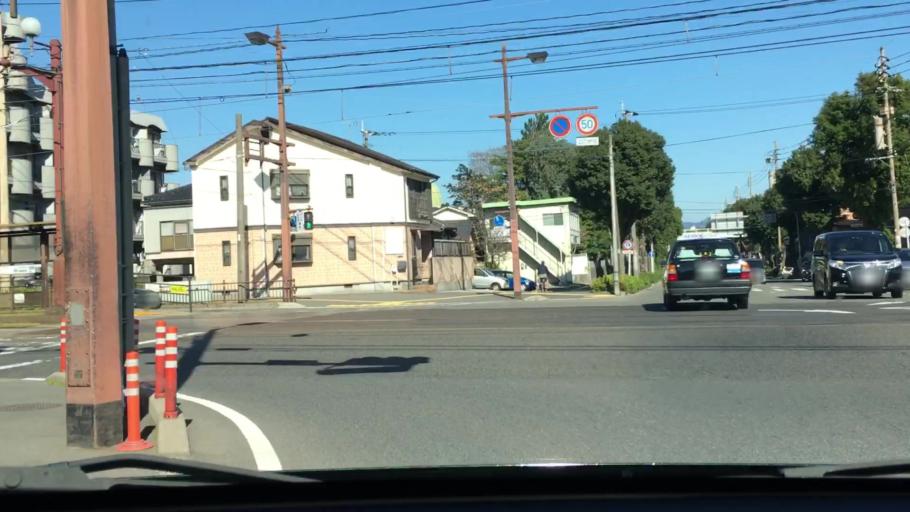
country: JP
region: Kagoshima
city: Kagoshima-shi
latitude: 31.5648
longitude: 130.5453
